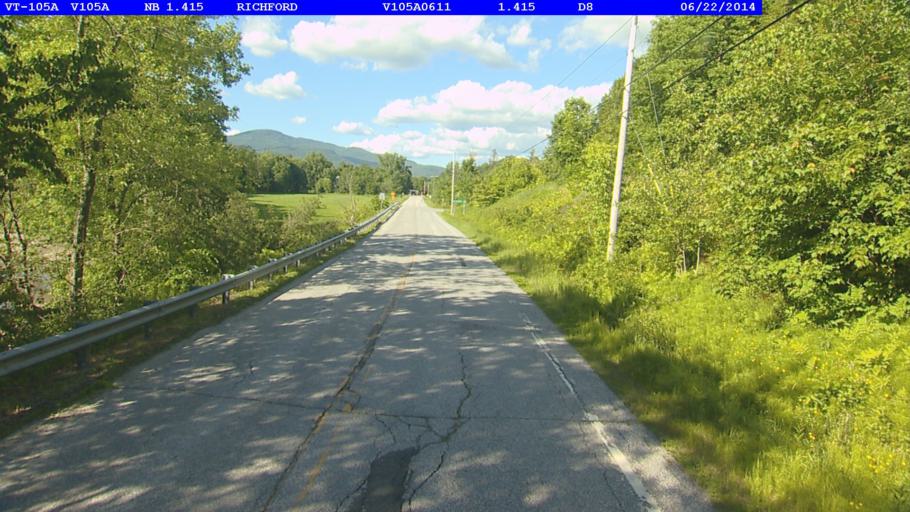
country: US
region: Vermont
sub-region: Franklin County
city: Richford
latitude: 45.0075
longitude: -72.5905
